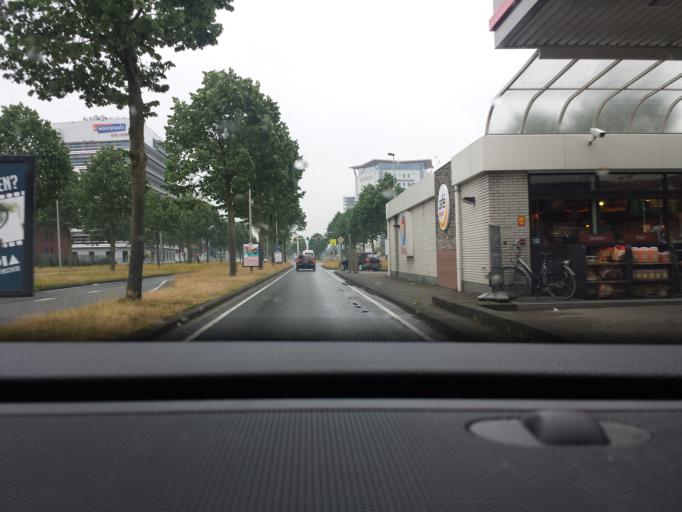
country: NL
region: Overijssel
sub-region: Gemeente Enschede
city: Enschede
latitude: 52.2080
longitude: 6.8895
